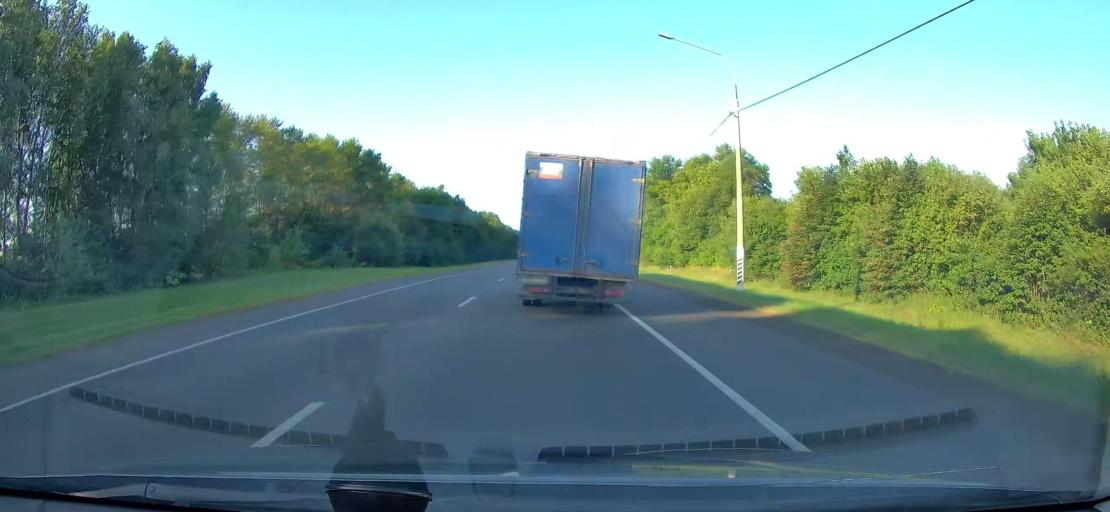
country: RU
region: Tula
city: Plavsk
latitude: 53.6361
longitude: 37.2092
